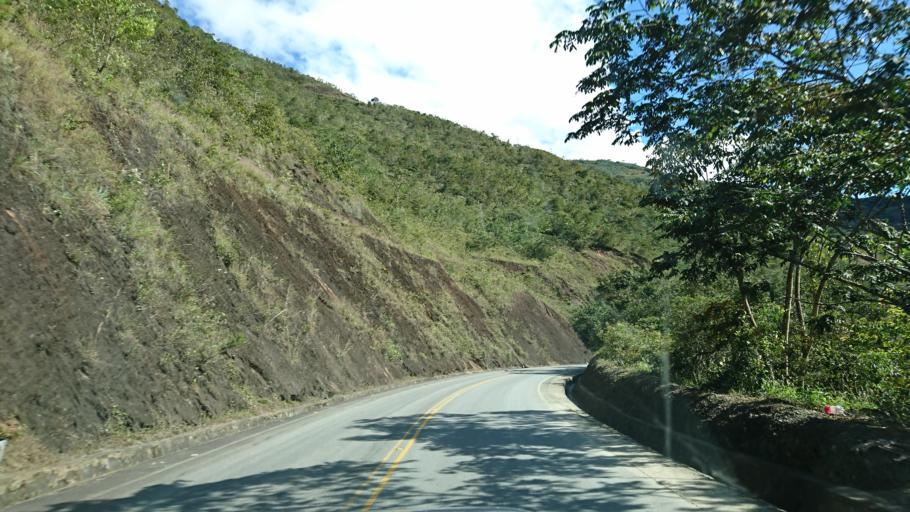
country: BO
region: La Paz
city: Coroico
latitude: -16.2024
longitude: -67.7666
